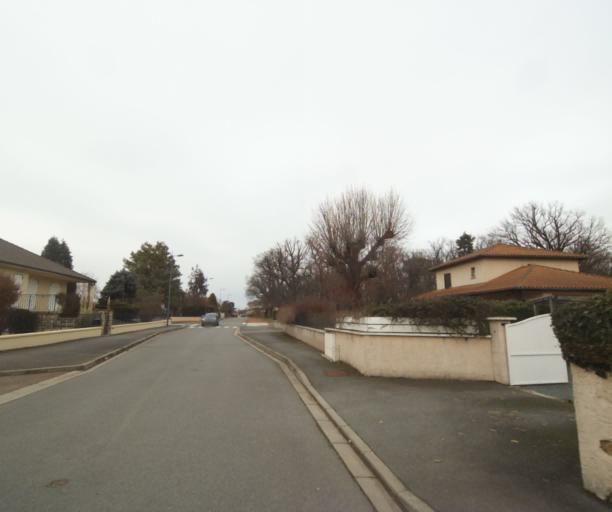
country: FR
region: Rhone-Alpes
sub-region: Departement de la Loire
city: Mably
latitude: 46.0628
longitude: 4.0741
